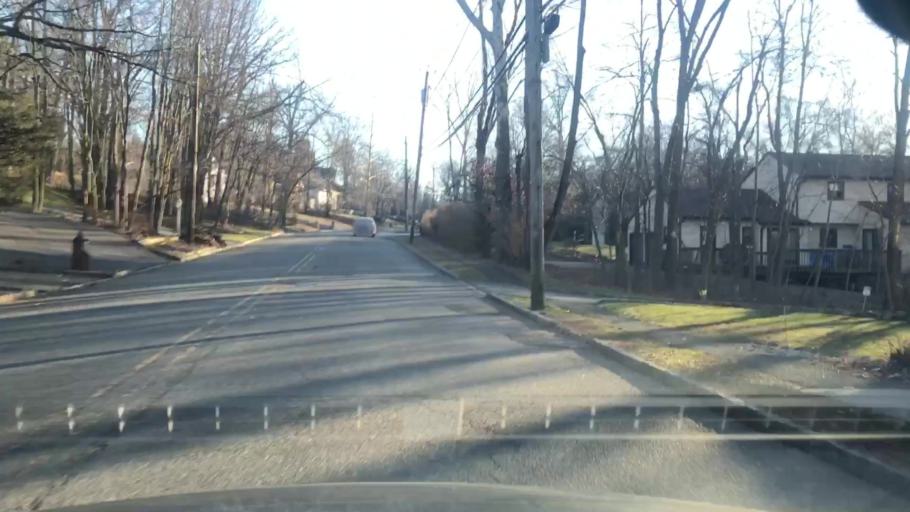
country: US
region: New Jersey
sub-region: Essex County
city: Northfield
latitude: 40.7754
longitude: -74.3074
